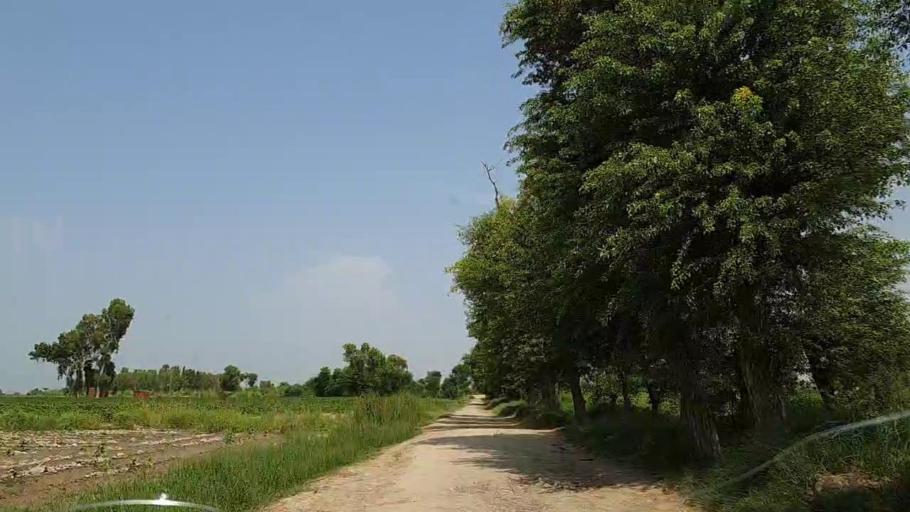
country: PK
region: Sindh
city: Adilpur
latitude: 27.9409
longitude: 69.3940
